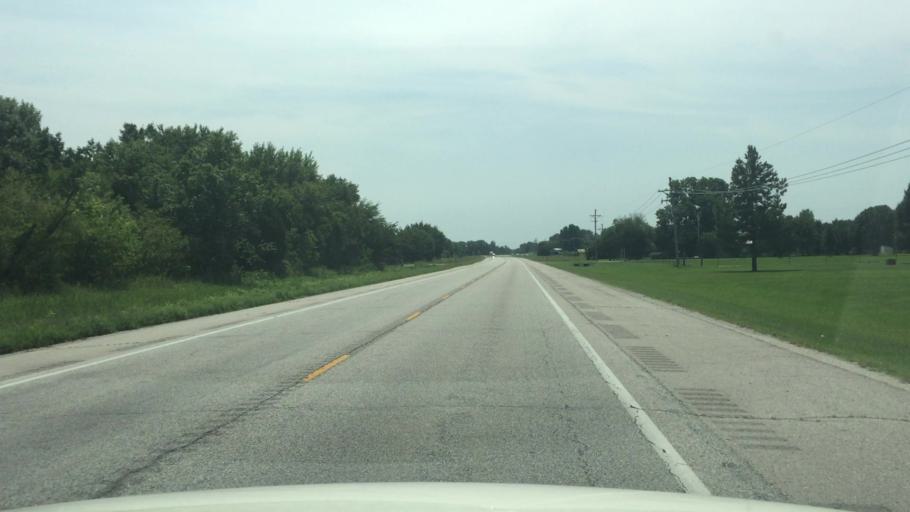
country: US
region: Kansas
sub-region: Cherokee County
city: Galena
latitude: 37.0953
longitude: -94.7045
